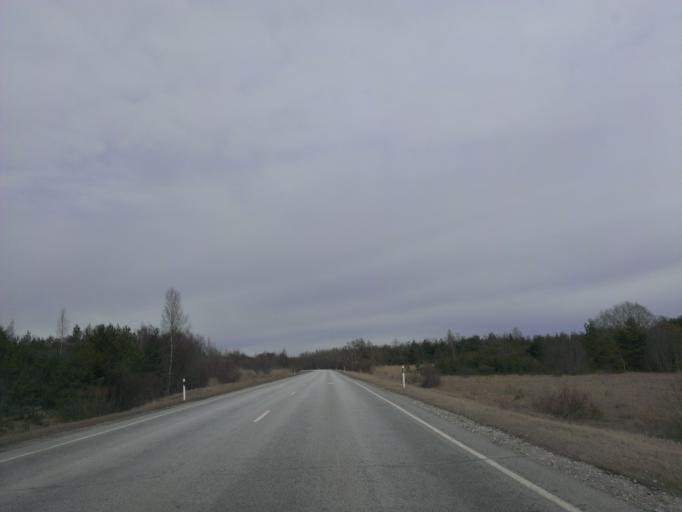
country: EE
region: Laeaene
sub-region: Lihula vald
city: Lihula
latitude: 58.5959
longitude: 23.5469
